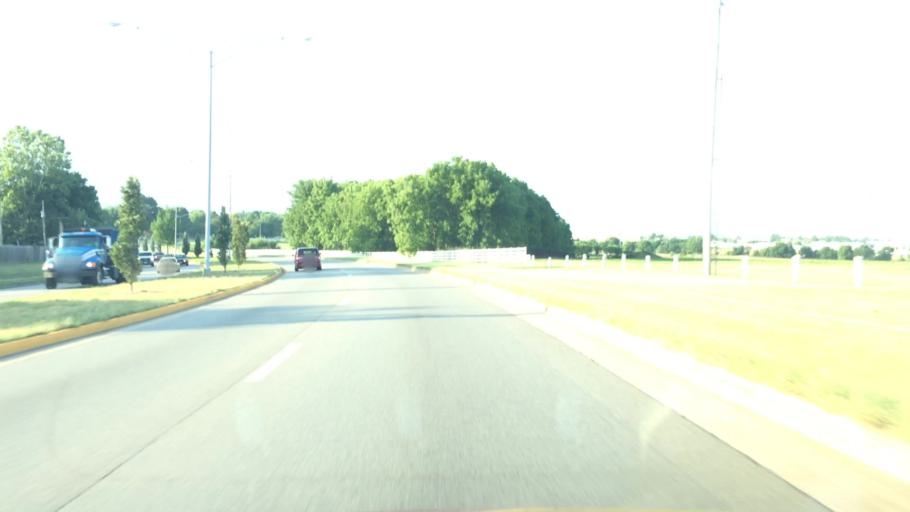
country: US
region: Missouri
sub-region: Greene County
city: Springfield
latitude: 37.1764
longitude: -93.3182
